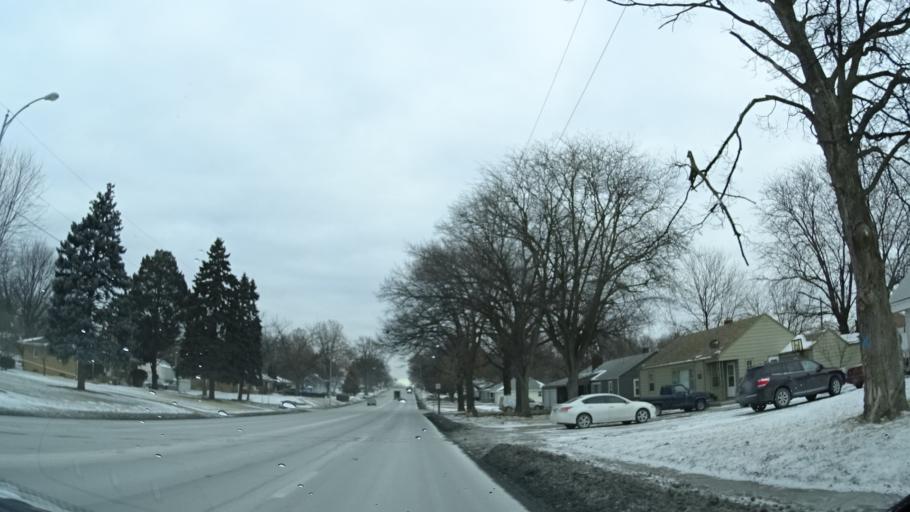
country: US
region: Nebraska
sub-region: Douglas County
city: Omaha
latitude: 41.2311
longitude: -95.9758
